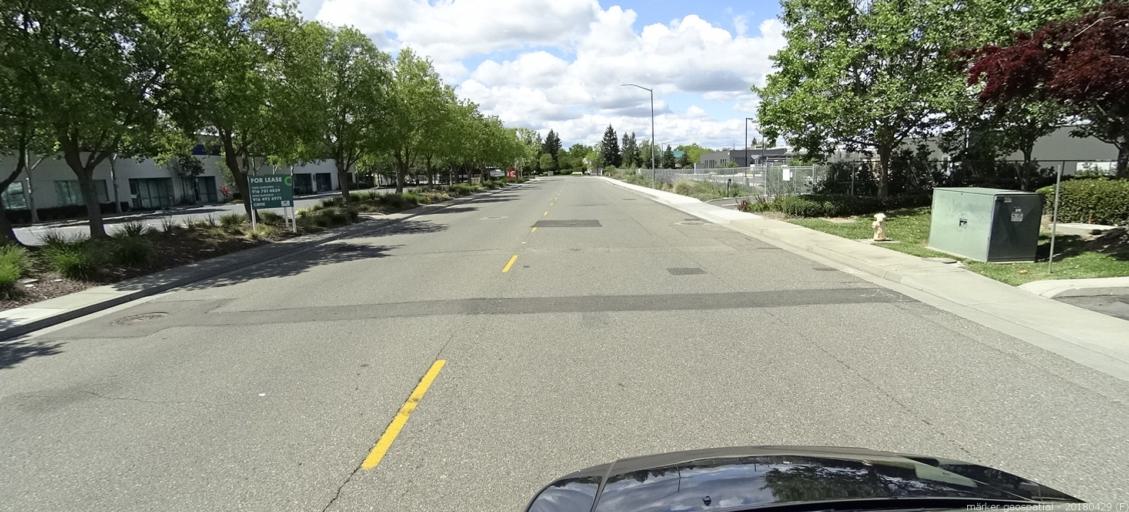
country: US
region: California
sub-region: Yolo County
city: West Sacramento
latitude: 38.5902
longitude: -121.5653
